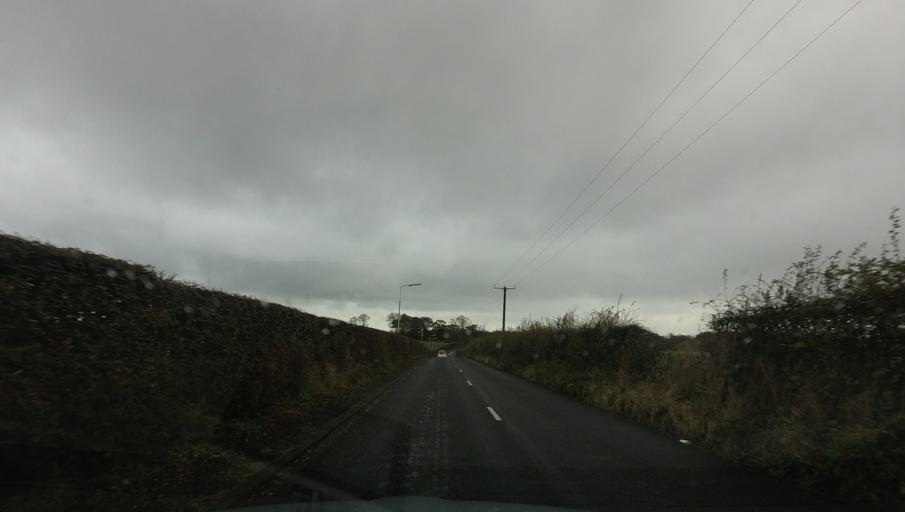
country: GB
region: Scotland
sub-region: Fife
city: East Wemyss
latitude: 56.1462
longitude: -3.0965
